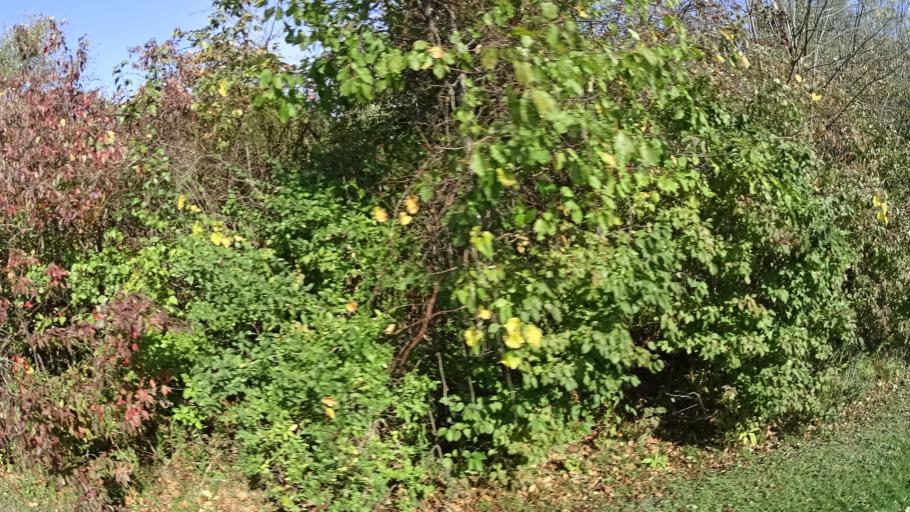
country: US
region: Ohio
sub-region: Lorain County
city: Vermilion-on-the-Lake
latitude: 41.4103
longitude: -82.3358
